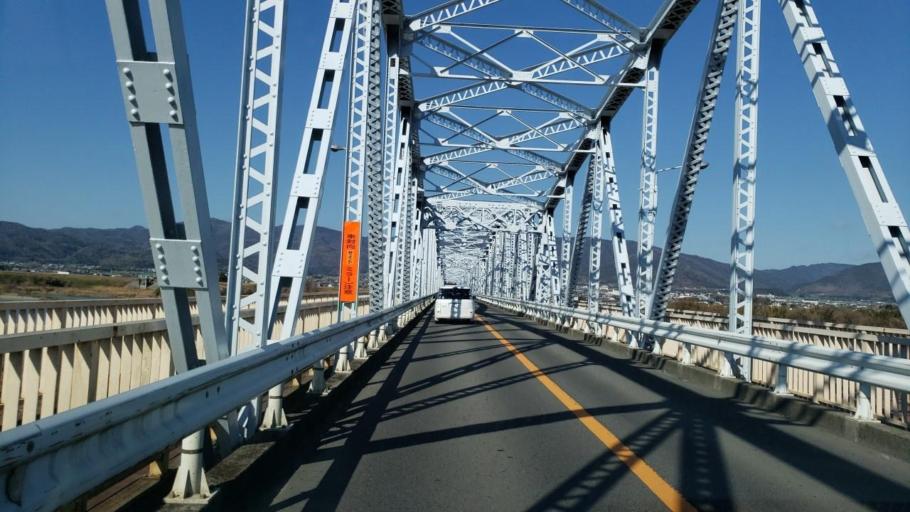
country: JP
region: Tokushima
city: Kamojimacho-jogejima
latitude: 34.0860
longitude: 134.3462
